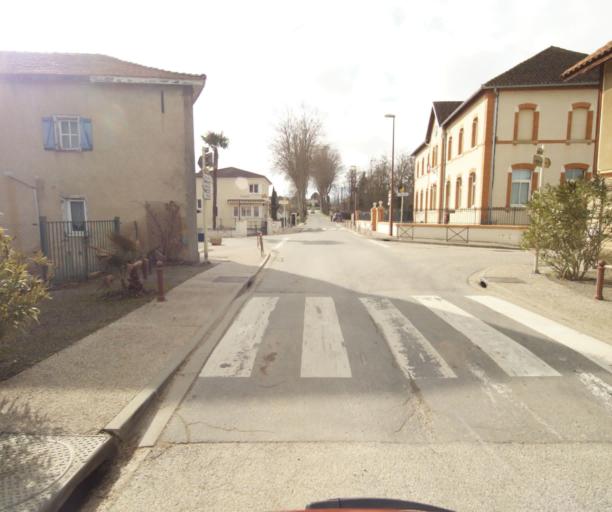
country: FR
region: Midi-Pyrenees
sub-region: Departement de l'Ariege
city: Pamiers
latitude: 43.1245
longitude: 1.5489
